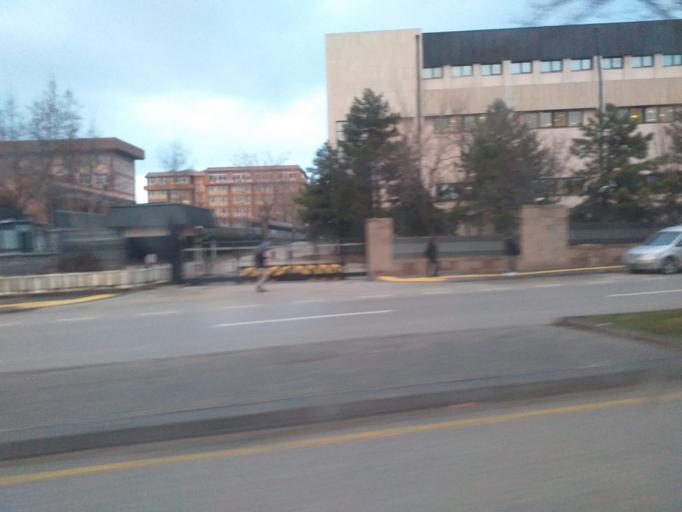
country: TR
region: Ankara
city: Ankara
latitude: 39.9334
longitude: 32.8281
